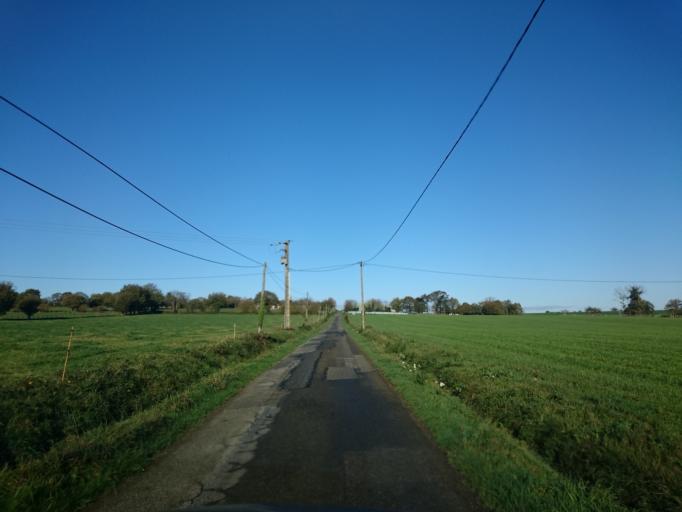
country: FR
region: Brittany
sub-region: Departement d'Ille-et-Vilaine
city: Corps-Nuds
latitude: 47.9541
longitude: -1.5601
